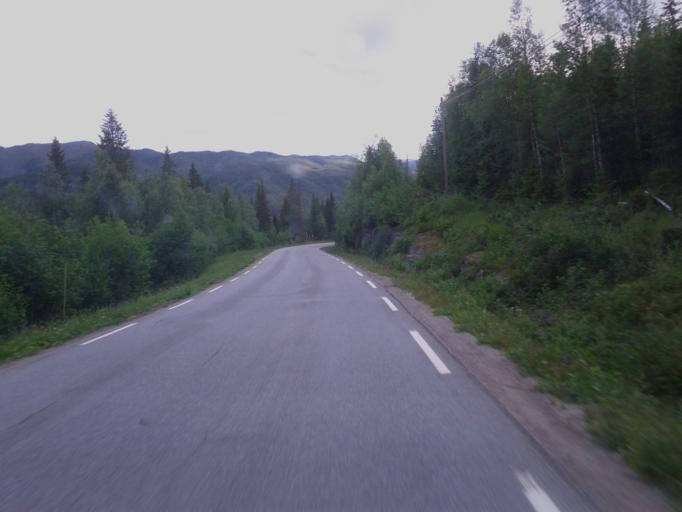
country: NO
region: Nordland
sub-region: Grane
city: Trofors
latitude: 65.5241
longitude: 13.6487
